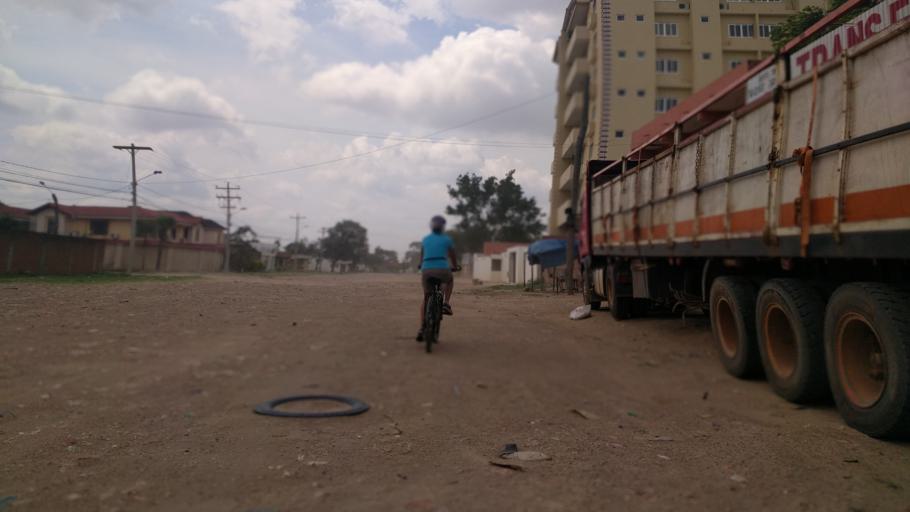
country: BO
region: Santa Cruz
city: Santa Cruz de la Sierra
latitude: -17.8027
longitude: -63.2216
